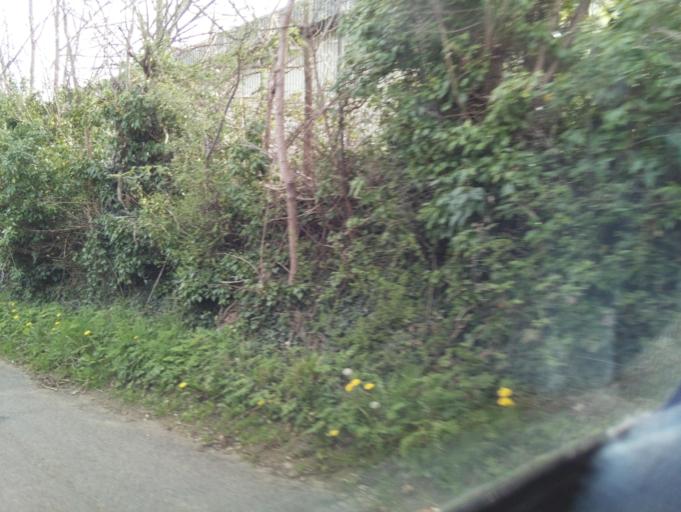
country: GB
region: England
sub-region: Dorset
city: Sherborne
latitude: 50.9559
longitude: -2.5066
